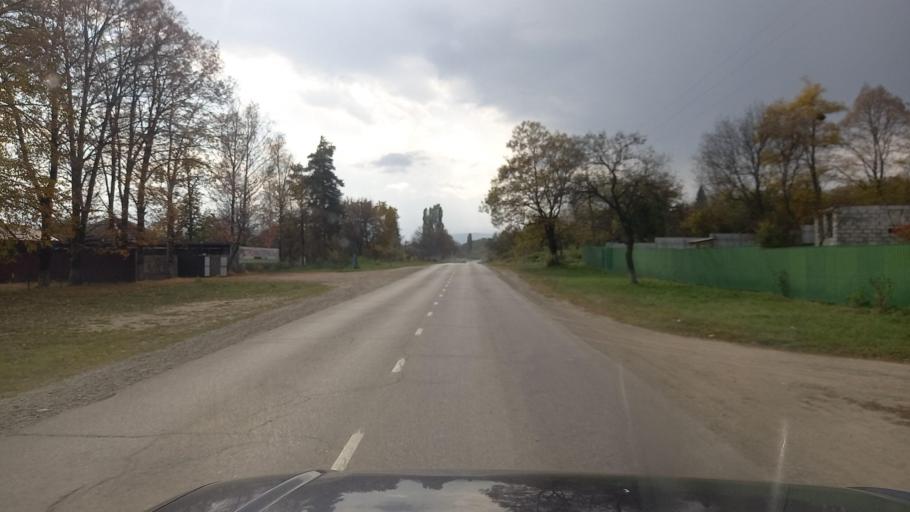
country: RU
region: Krasnodarskiy
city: Psebay
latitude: 44.1350
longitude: 40.8152
